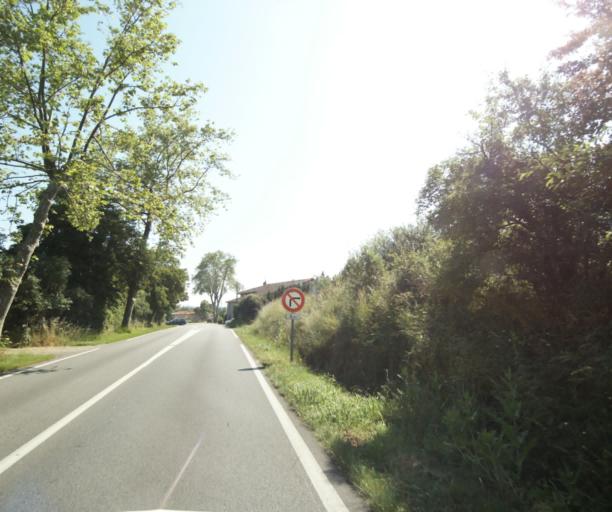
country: FR
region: Midi-Pyrenees
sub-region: Departement du Tarn-et-Garonne
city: Montbeton
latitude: 43.9888
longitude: 1.3081
